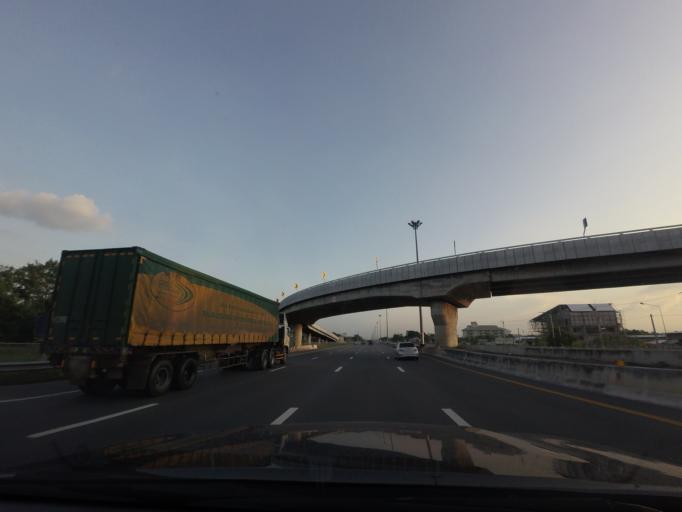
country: TH
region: Pathum Thani
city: Khlong Luang
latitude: 14.0798
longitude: 100.6954
